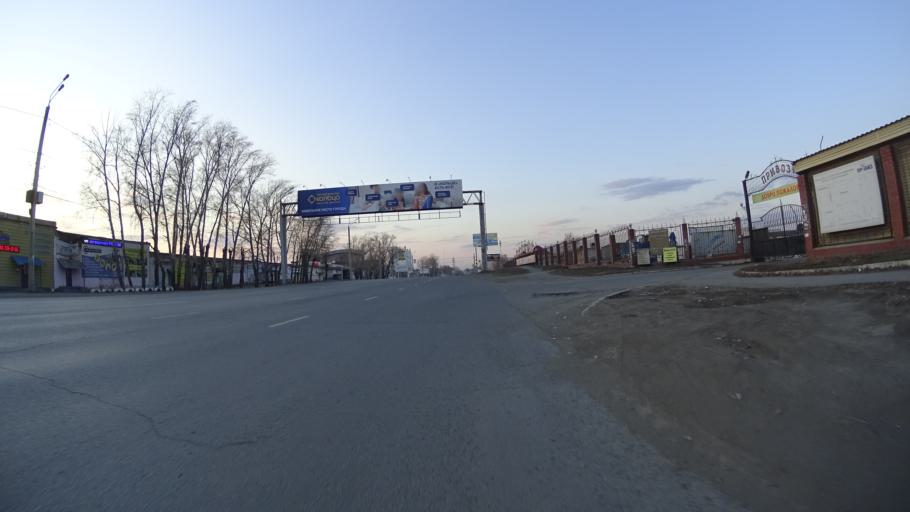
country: RU
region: Chelyabinsk
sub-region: Gorod Chelyabinsk
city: Chelyabinsk
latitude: 55.1093
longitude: 61.3871
